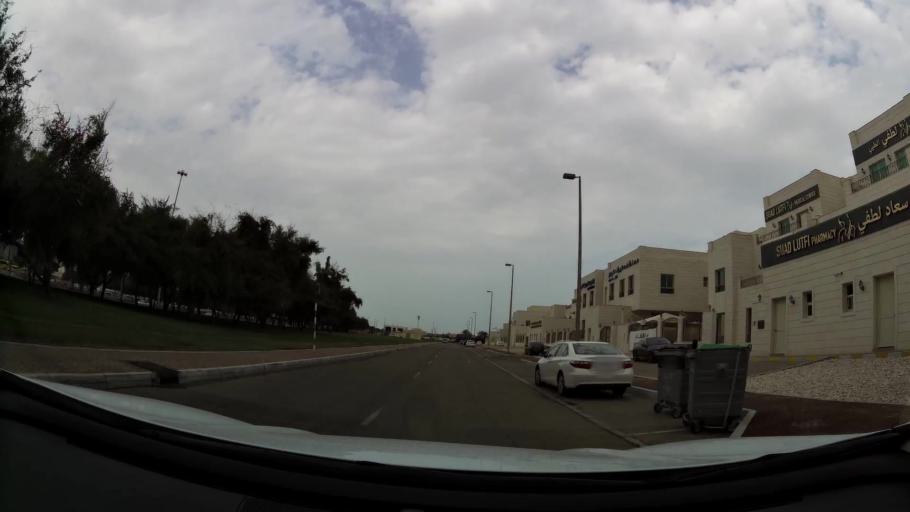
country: AE
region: Abu Dhabi
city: Abu Dhabi
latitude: 24.4234
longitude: 54.4560
